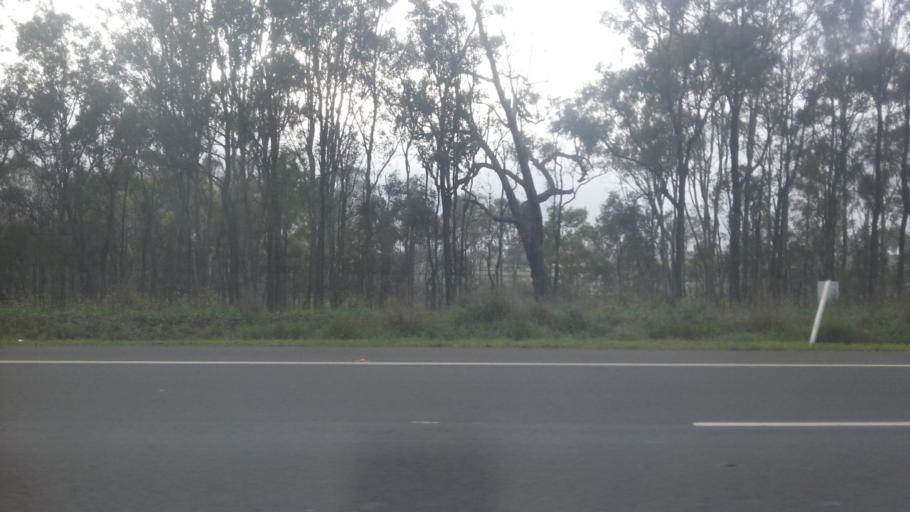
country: AU
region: New South Wales
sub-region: Penrith Municipality
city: Glenmore Park
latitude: -33.8062
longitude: 150.6958
